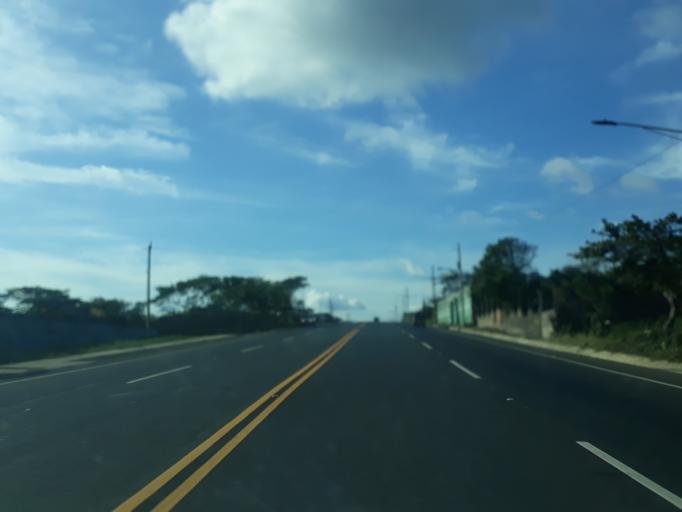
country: NI
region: Managua
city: El Crucero
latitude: 11.9601
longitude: -86.3042
